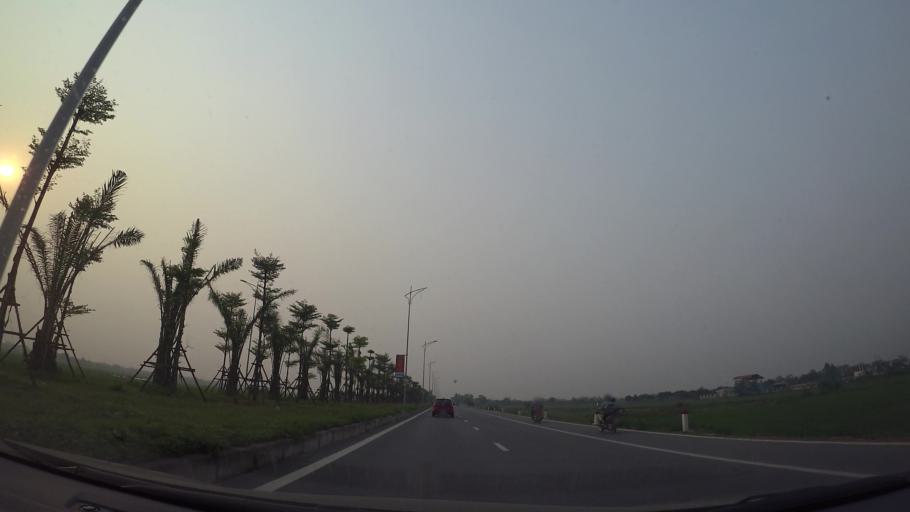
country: VN
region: Ha Noi
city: Kim Bai
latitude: 20.8785
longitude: 105.8005
